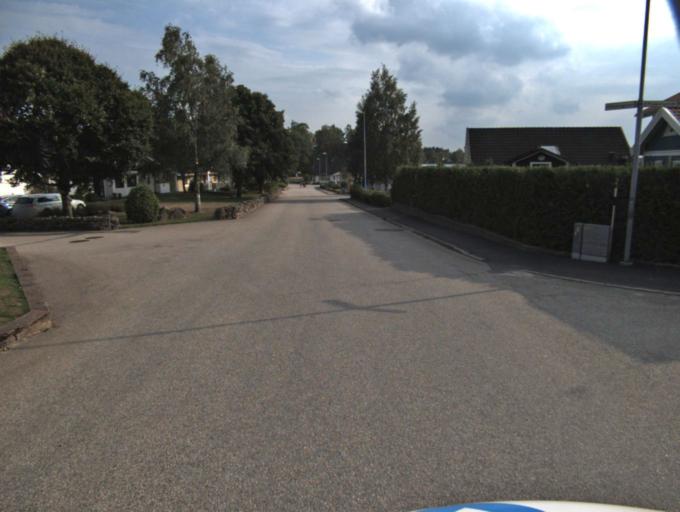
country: SE
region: Vaestra Goetaland
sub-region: Ulricehamns Kommun
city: Ulricehamn
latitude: 57.7835
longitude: 13.4271
